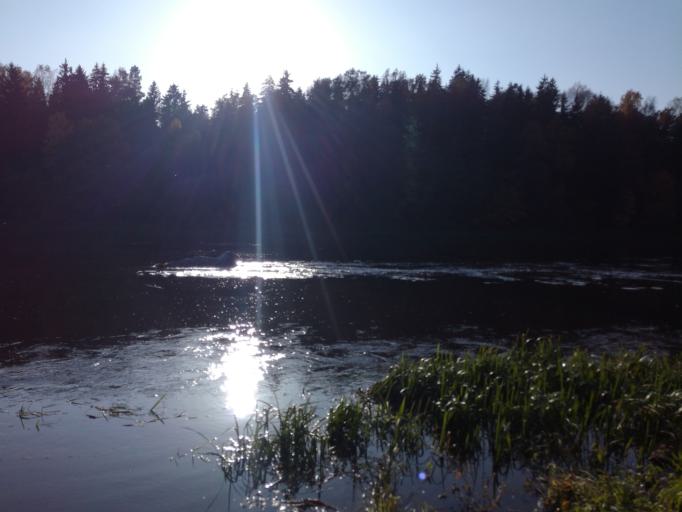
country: LT
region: Alytaus apskritis
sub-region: Alytus
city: Alytus
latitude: 54.3916
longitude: 24.0852
